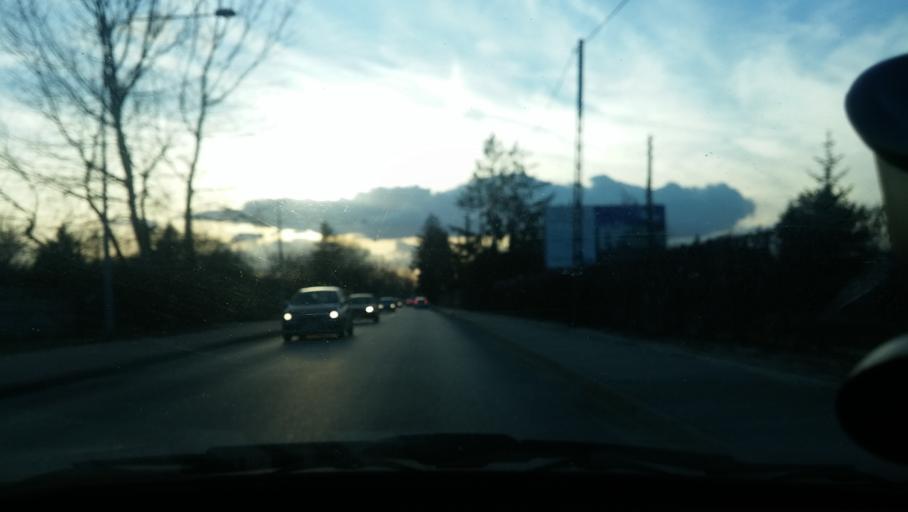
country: PL
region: Masovian Voivodeship
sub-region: Warszawa
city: Wawer
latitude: 52.1846
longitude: 21.1380
